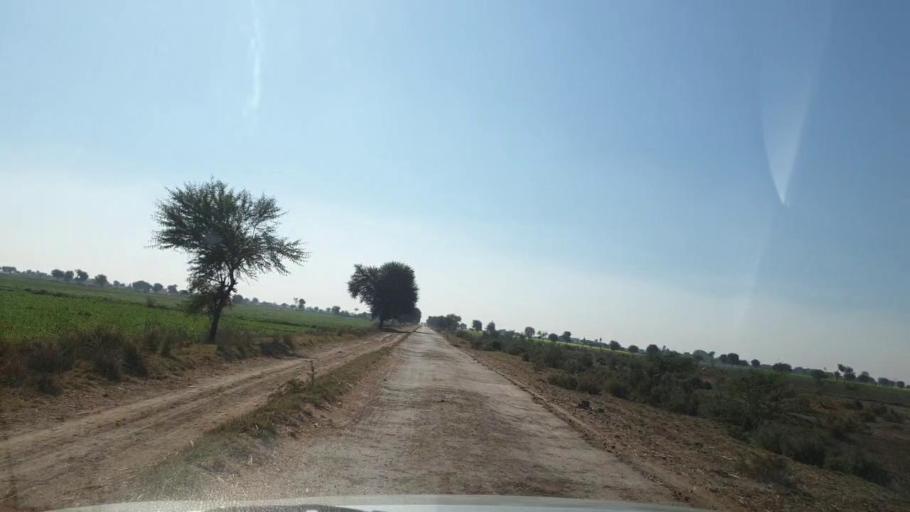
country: PK
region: Sindh
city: Jhol
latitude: 25.8186
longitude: 69.0358
